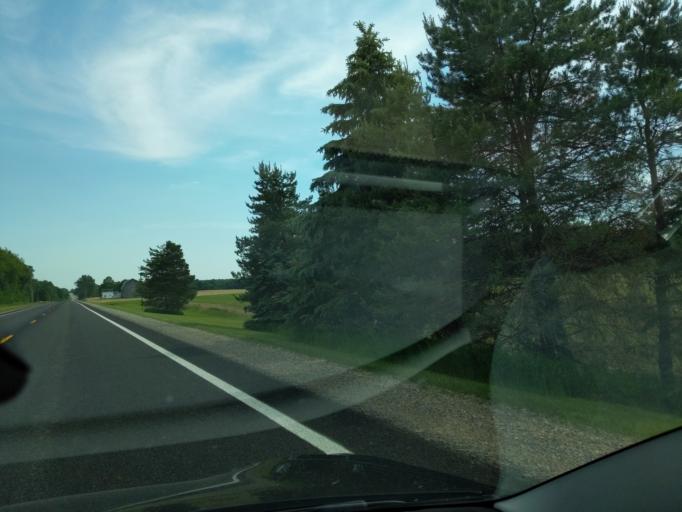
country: US
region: Michigan
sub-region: Barry County
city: Nashville
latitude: 42.6924
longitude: -85.0952
